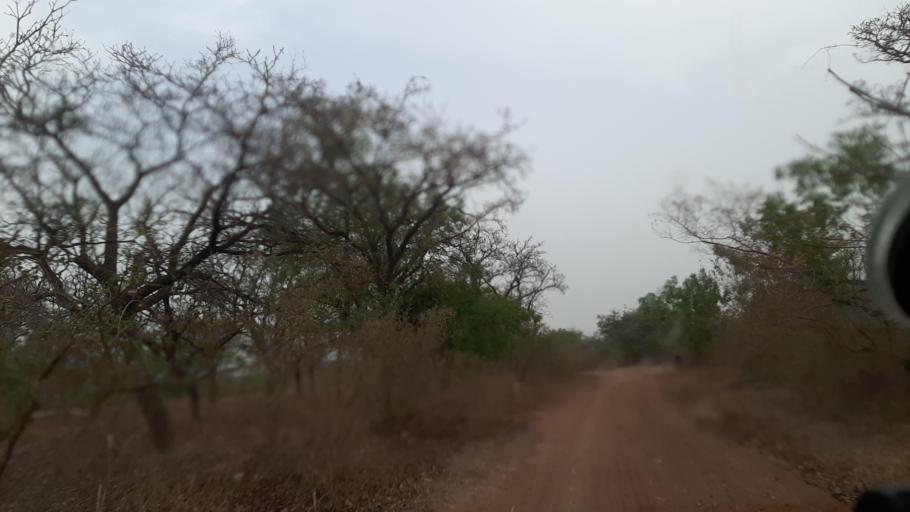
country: BF
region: Boucle du Mouhoun
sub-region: Province des Banwa
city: Salanso
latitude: 11.8481
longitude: -4.4206
